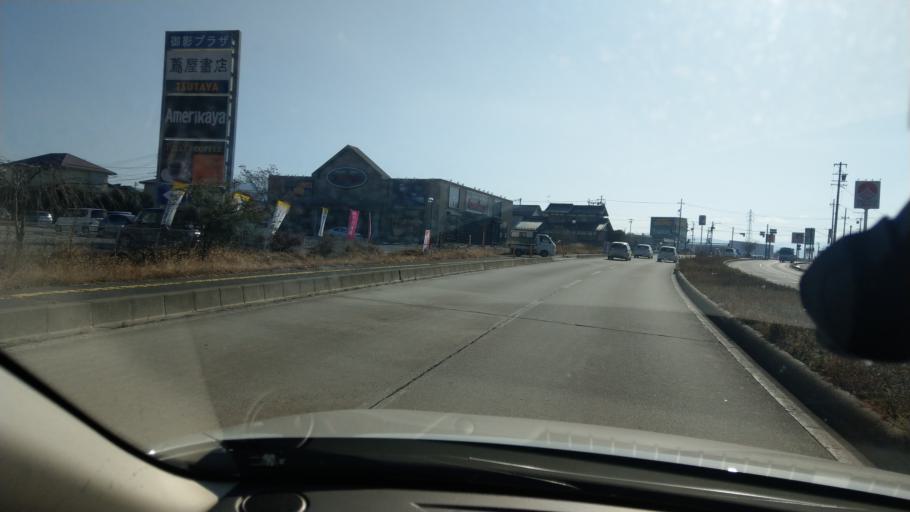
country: JP
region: Nagano
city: Komoro
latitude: 36.3009
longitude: 138.4664
